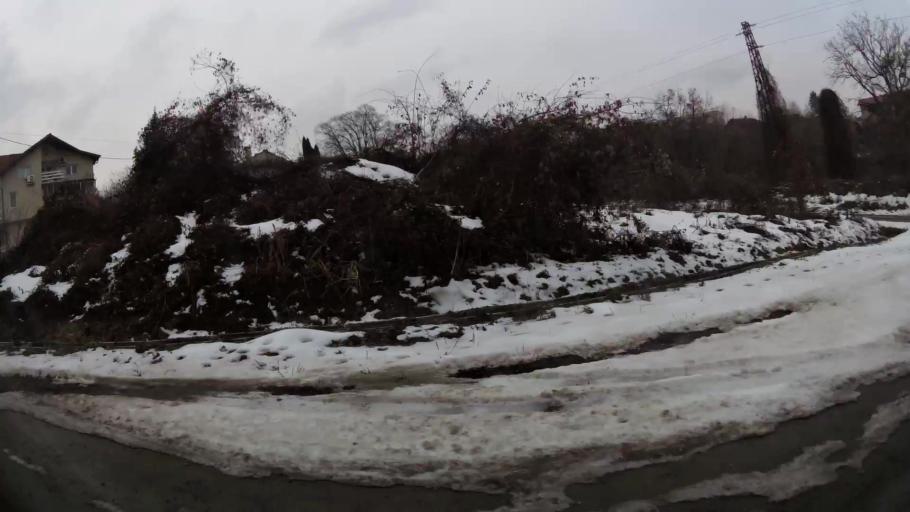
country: BG
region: Sofiya
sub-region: Obshtina Bozhurishte
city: Bozhurishte
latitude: 42.6735
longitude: 23.2339
